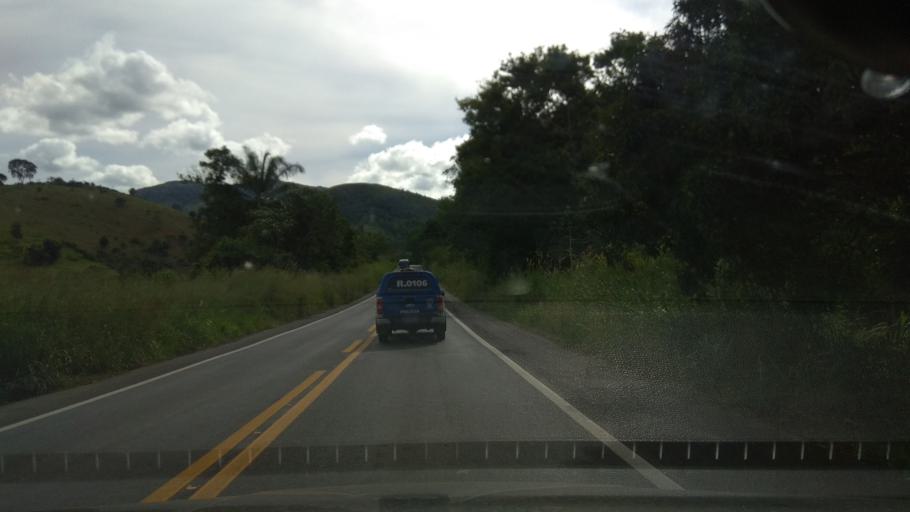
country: BR
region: Bahia
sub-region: Jitauna
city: Jitauna
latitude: -14.0076
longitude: -39.9171
